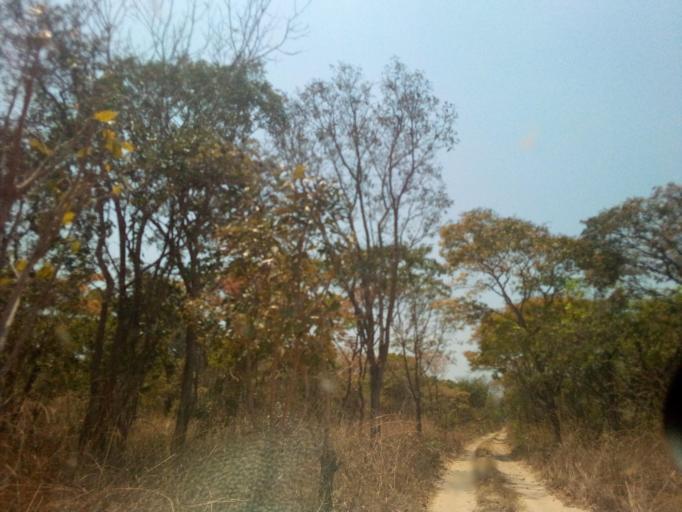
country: ZM
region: Copperbelt
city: Kataba
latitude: -12.2514
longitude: 30.3907
